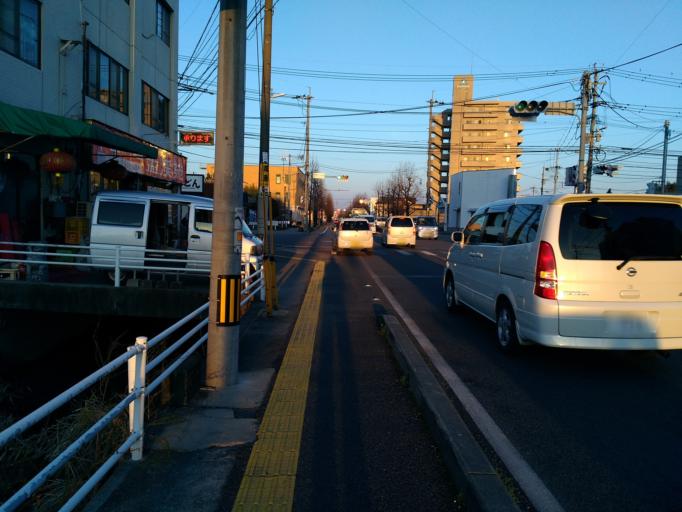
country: JP
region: Saga Prefecture
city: Saga-shi
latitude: 33.2609
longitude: 130.3035
